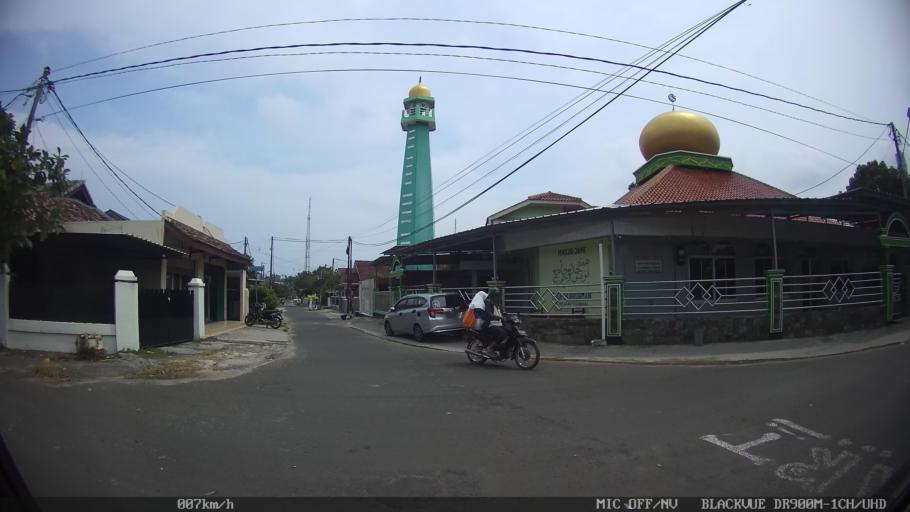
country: ID
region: Lampung
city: Bandarlampung
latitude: -5.4183
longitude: 105.2649
